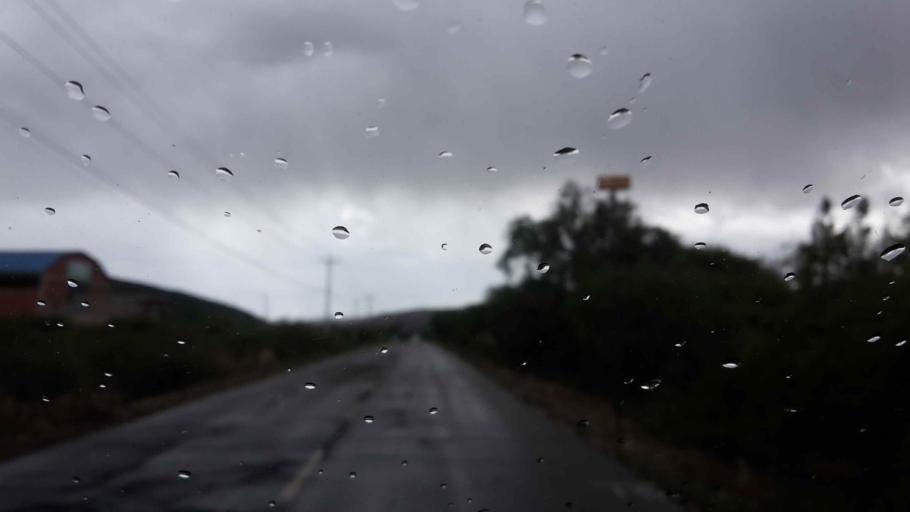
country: BO
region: Cochabamba
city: Tarata
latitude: -17.5716
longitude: -66.0679
